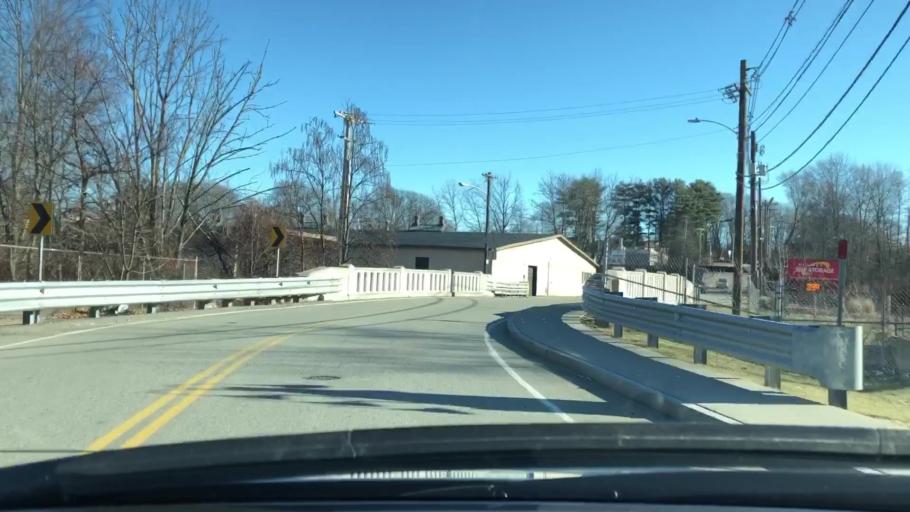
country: US
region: Massachusetts
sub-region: Norfolk County
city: Norwood
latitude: 42.1730
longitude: -71.2051
